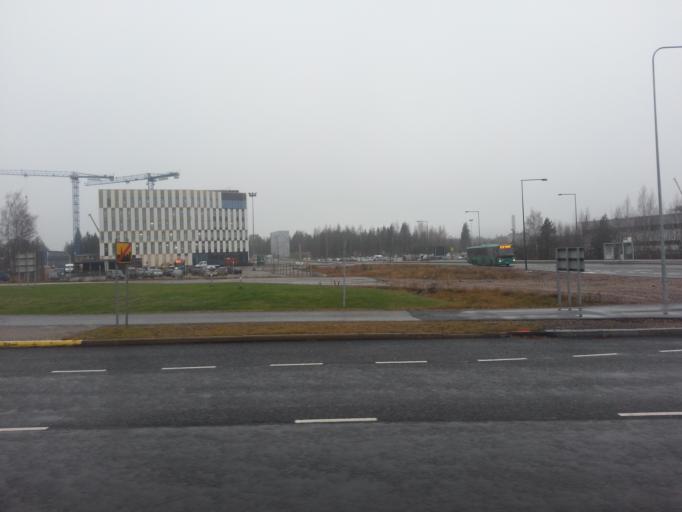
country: FI
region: Uusimaa
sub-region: Helsinki
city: Vantaa
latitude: 60.3082
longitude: 24.9618
